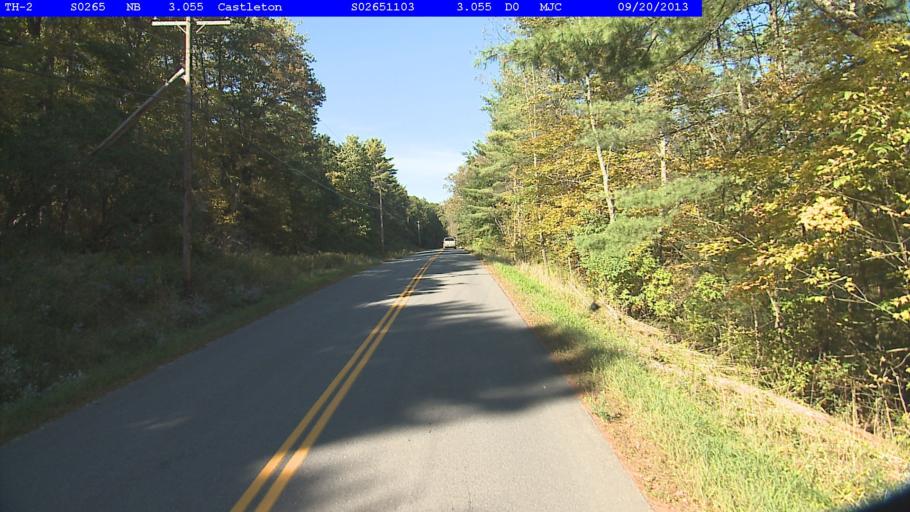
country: US
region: Vermont
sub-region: Rutland County
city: Fair Haven
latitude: 43.6447
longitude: -73.2331
